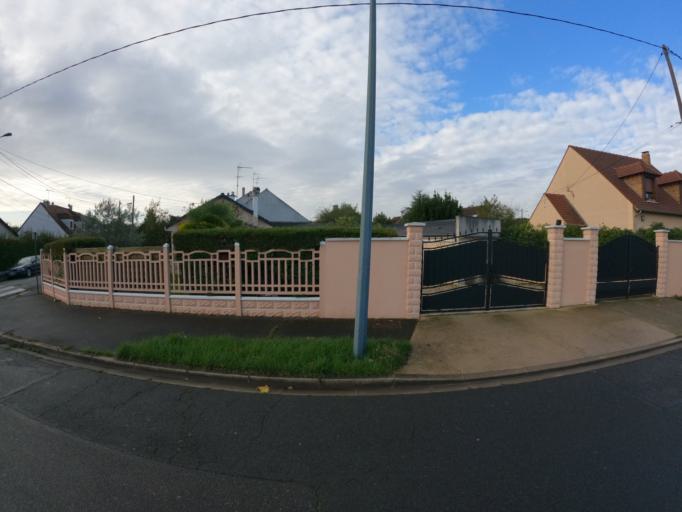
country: FR
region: Ile-de-France
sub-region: Departement de Seine-et-Marne
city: Le Pin
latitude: 48.8997
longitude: 2.6168
